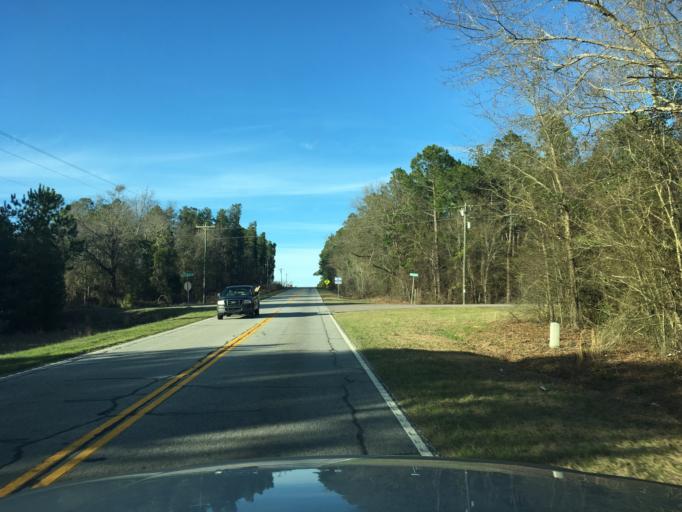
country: US
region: South Carolina
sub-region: Edgefield County
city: Johnston
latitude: 33.7479
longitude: -81.6437
